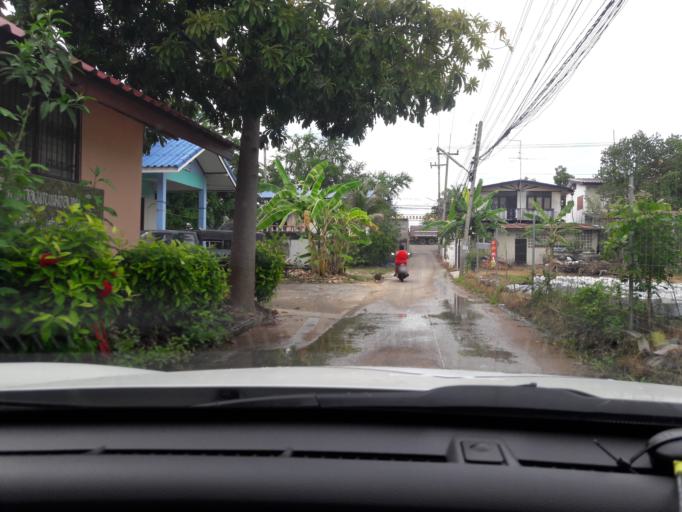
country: TH
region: Nakhon Sawan
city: Tak Fa
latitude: 15.3494
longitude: 100.5003
